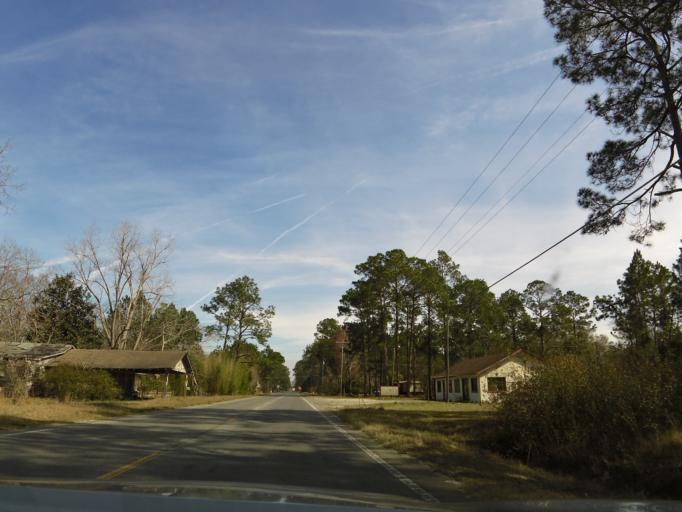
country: US
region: Georgia
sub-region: Ware County
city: Deenwood
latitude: 31.1593
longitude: -82.4295
